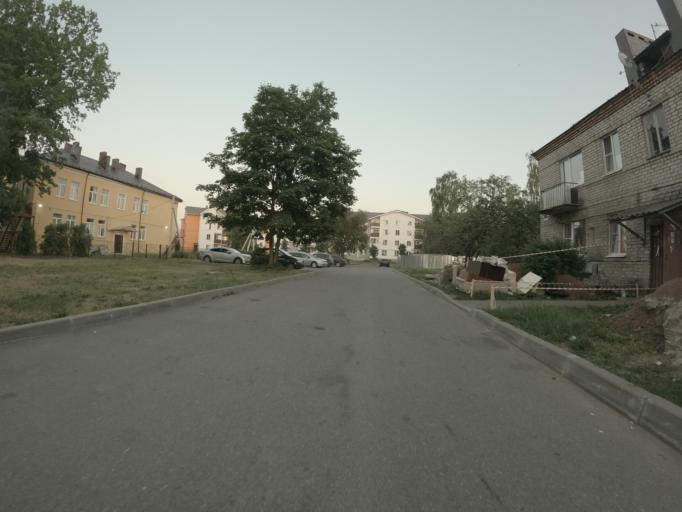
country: RU
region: Leningrad
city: Pavlovo
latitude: 59.8466
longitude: 30.9348
